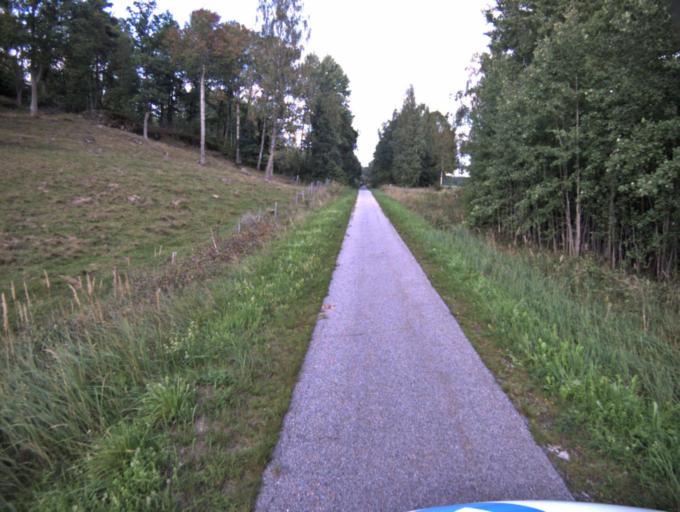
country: SE
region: Vaestra Goetaland
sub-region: Ulricehamns Kommun
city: Ulricehamn
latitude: 57.8889
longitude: 13.4358
